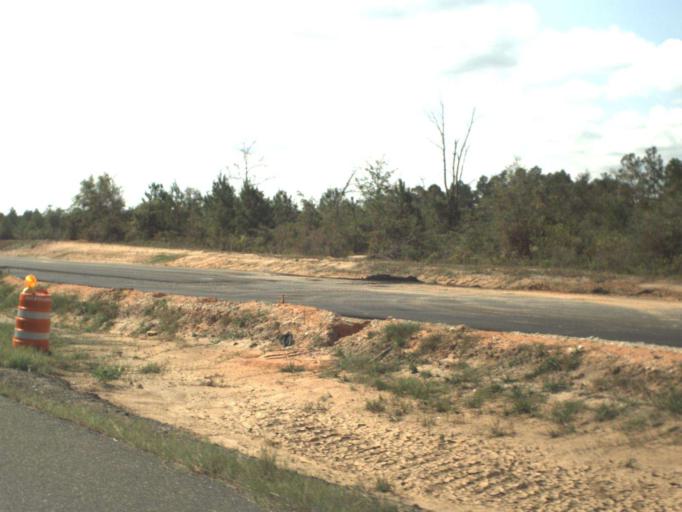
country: US
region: Florida
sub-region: Holmes County
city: Bonifay
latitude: 30.6662
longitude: -85.6912
